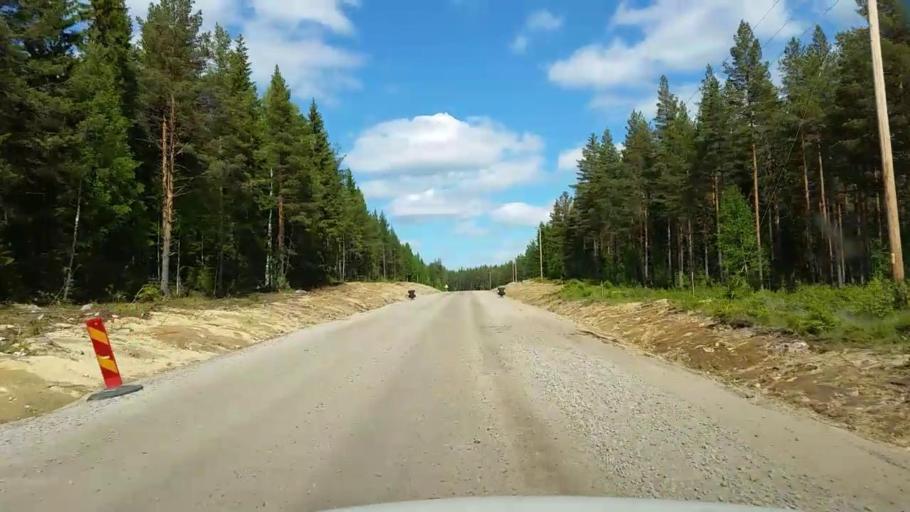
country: SE
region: Gaevleborg
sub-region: Ljusdals Kommun
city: Farila
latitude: 61.5844
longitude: 15.9087
